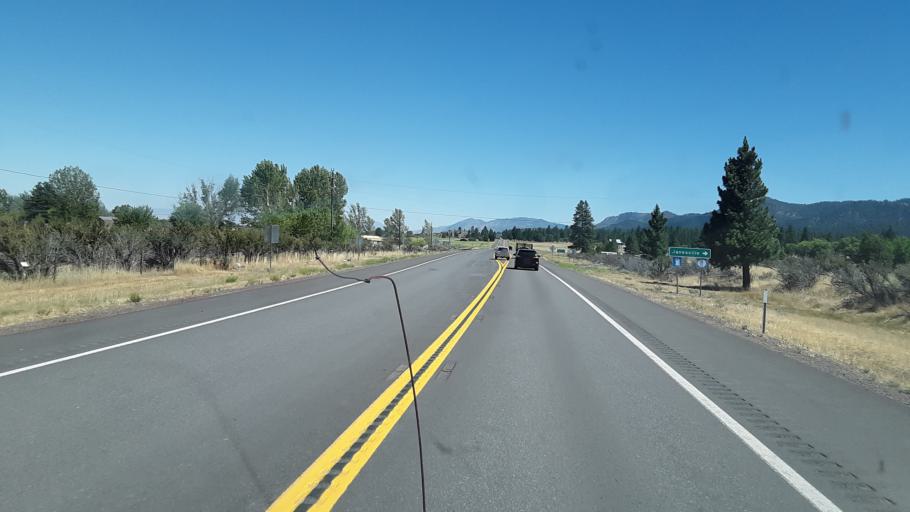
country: US
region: California
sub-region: Lassen County
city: Janesville
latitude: 40.3165
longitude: -120.5414
